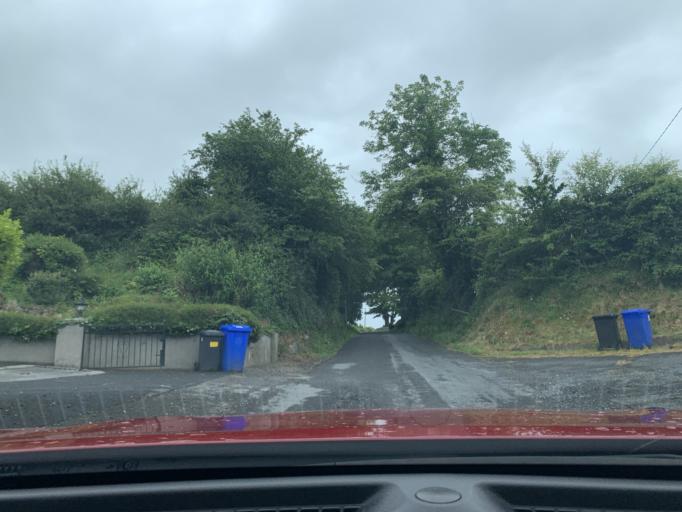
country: IE
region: Connaught
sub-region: Sligo
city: Sligo
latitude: 54.3132
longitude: -8.4775
